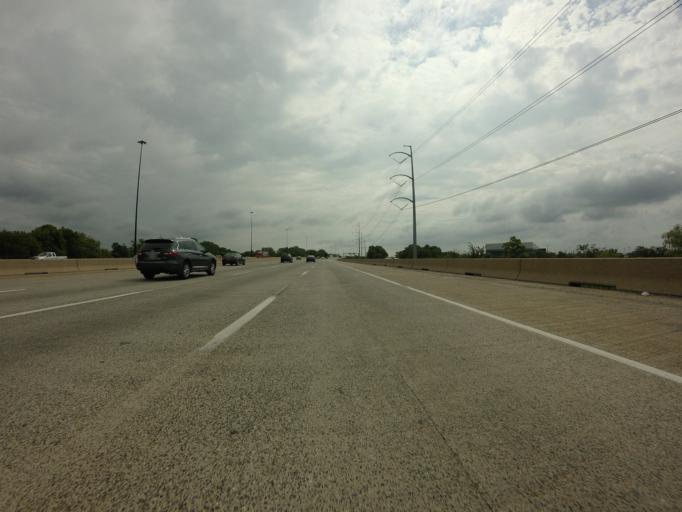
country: US
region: Pennsylvania
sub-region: Delaware County
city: Folcroft
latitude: 39.8759
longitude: -75.2708
